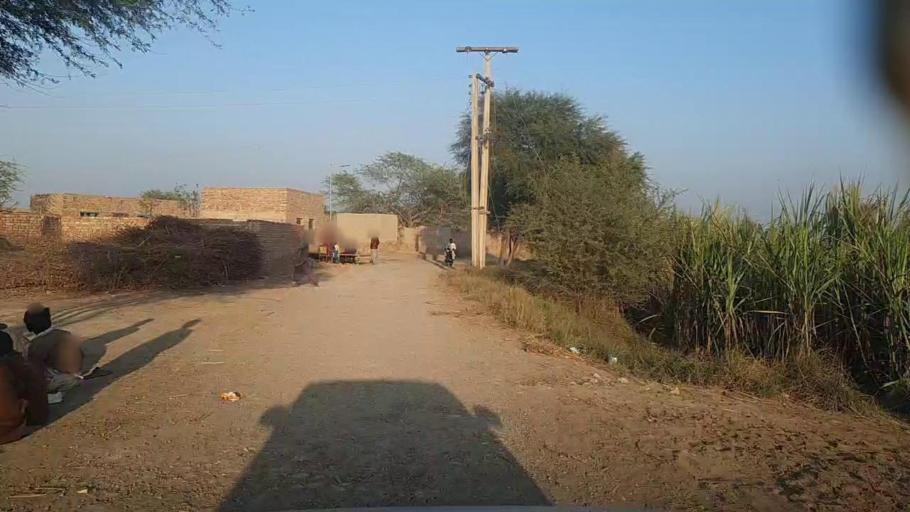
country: PK
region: Sindh
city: Khairpur
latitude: 28.0605
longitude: 69.7561
